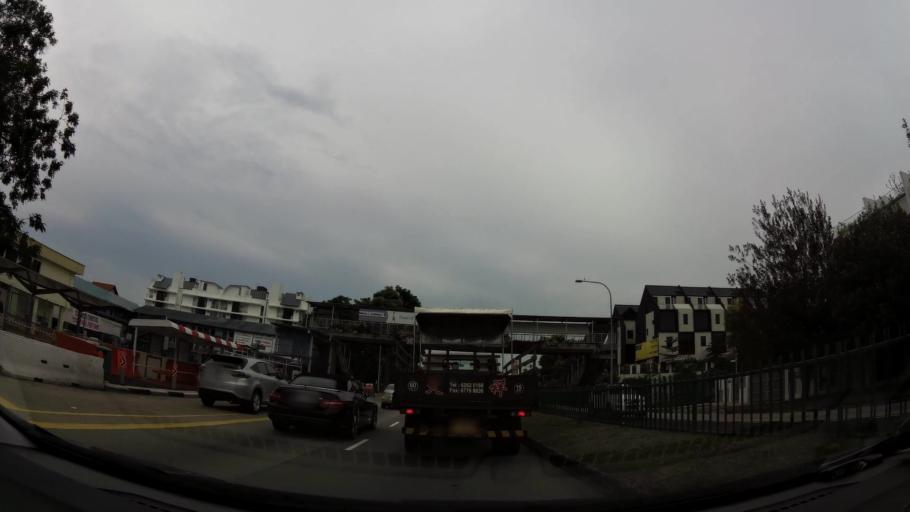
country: SG
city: Singapore
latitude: 1.3569
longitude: 103.8816
